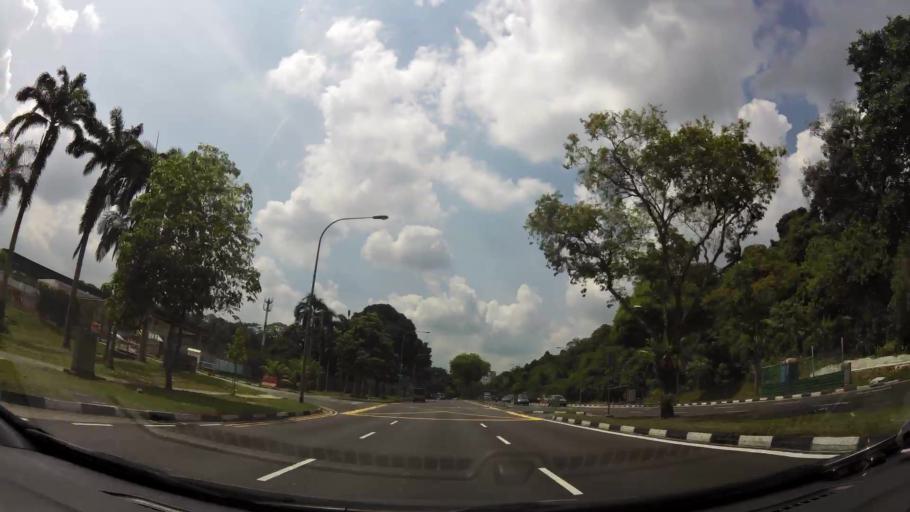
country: MY
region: Johor
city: Johor Bahru
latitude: 1.4104
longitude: 103.7749
